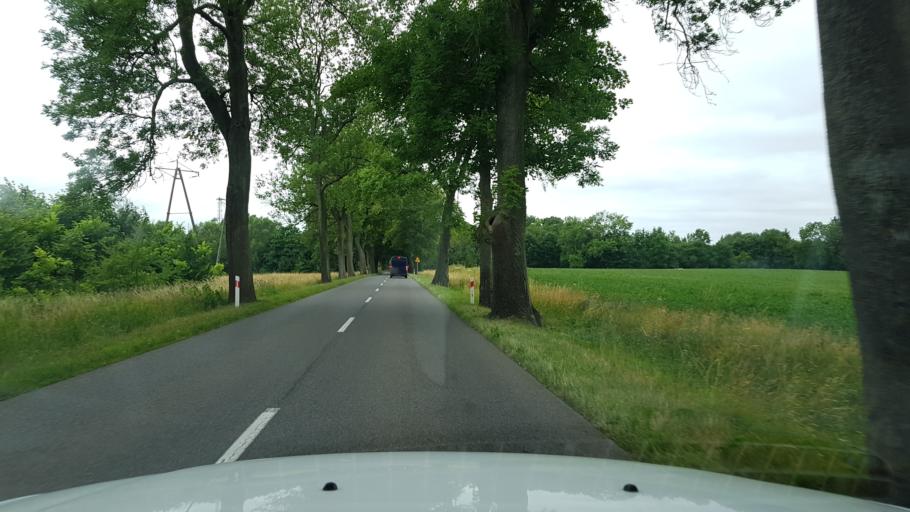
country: PL
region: West Pomeranian Voivodeship
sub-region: Powiat kamienski
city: Kamien Pomorski
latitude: 53.9614
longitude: 14.7998
